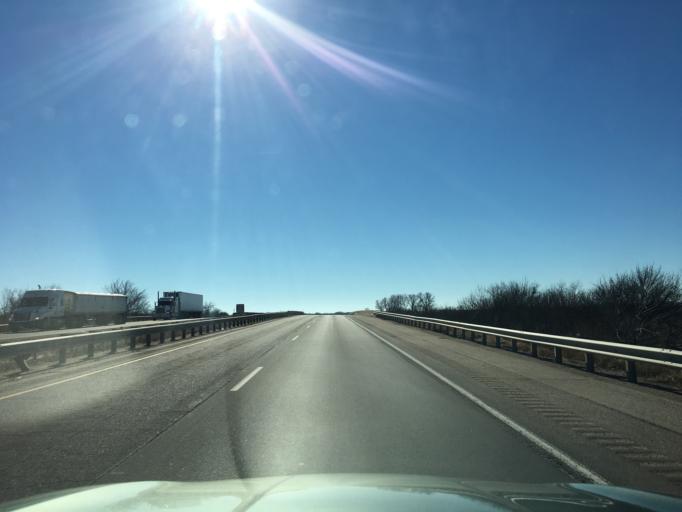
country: US
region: Oklahoma
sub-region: Kay County
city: Blackwell
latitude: 36.9352
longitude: -97.3478
